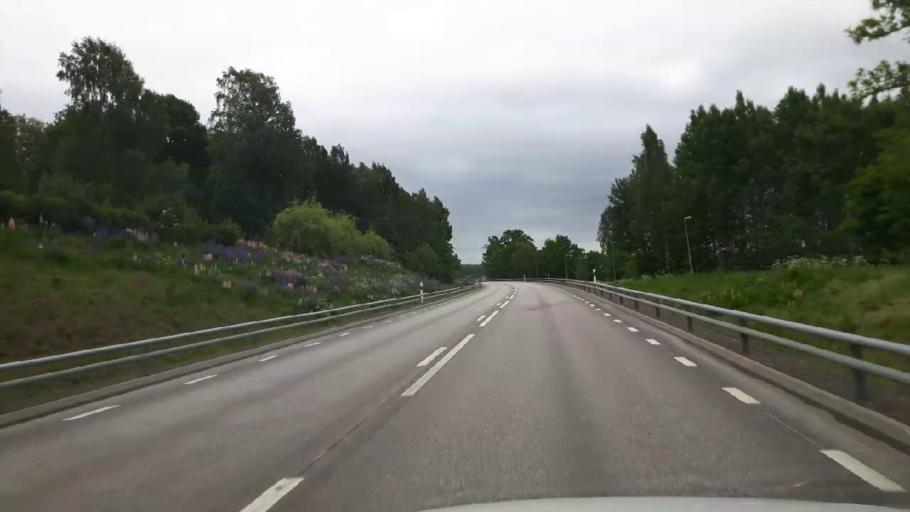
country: SE
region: Vaestmanland
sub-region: Kopings Kommun
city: Kolsva
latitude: 59.5572
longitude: 15.8952
